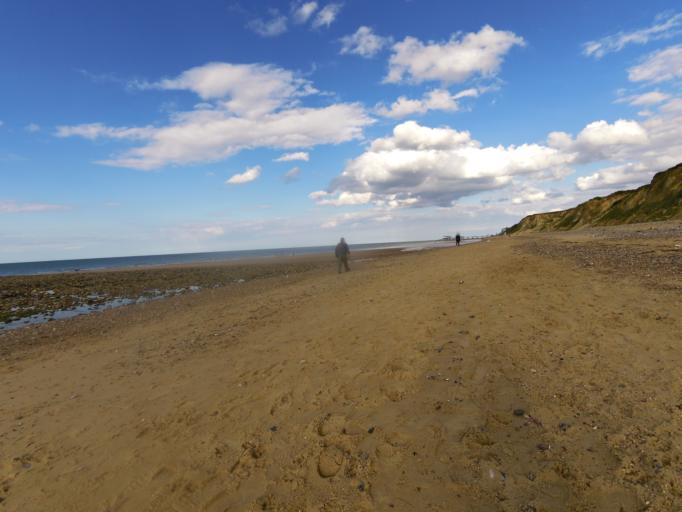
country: GB
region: England
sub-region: Norfolk
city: Cromer
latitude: 52.9365
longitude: 1.2799
